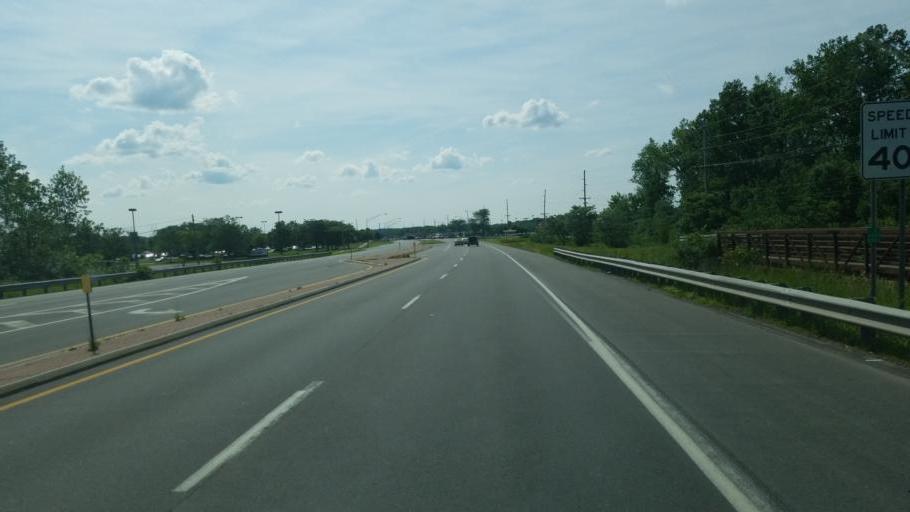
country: US
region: New York
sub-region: Ontario County
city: Canandaigua
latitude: 42.8767
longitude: -77.2506
